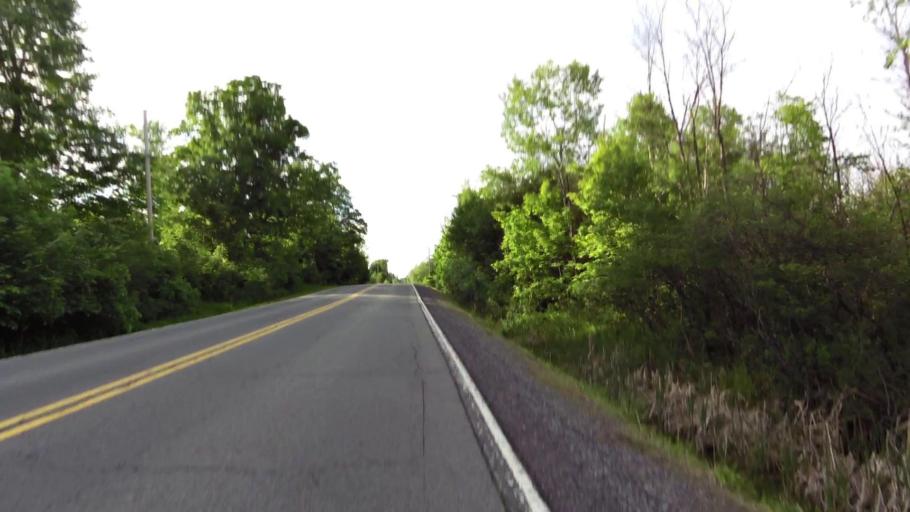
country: CA
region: Ontario
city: Ottawa
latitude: 45.2273
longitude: -75.6068
